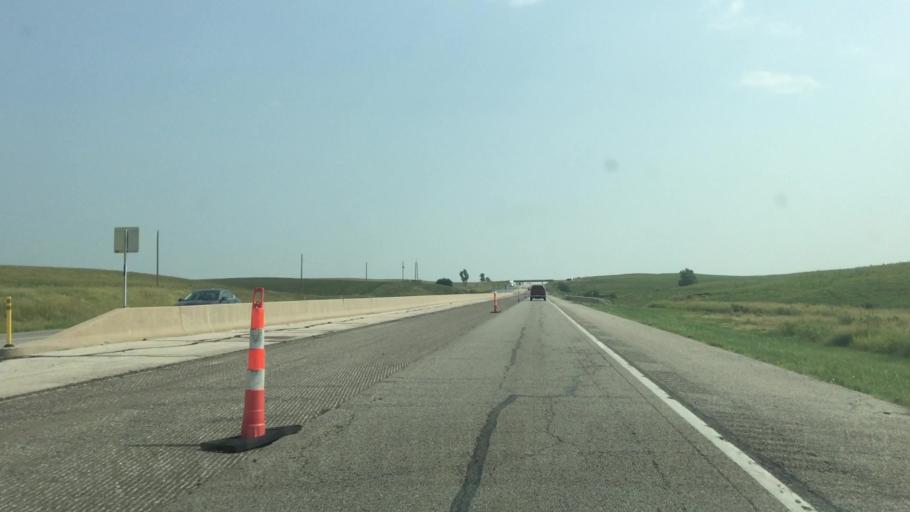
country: US
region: Kansas
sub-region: Chase County
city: Cottonwood Falls
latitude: 38.1537
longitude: -96.4912
